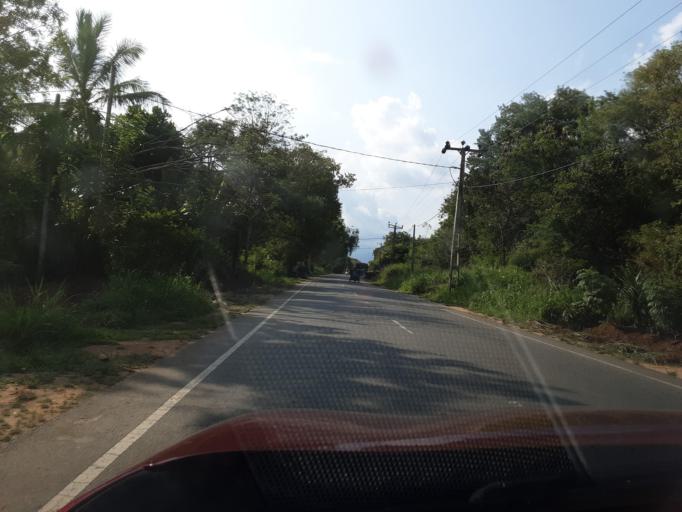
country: LK
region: Uva
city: Haputale
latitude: 6.6130
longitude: 81.1314
